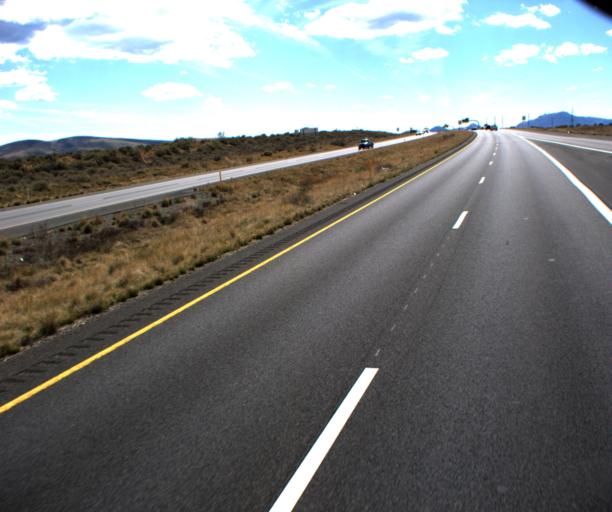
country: US
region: Arizona
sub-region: Yavapai County
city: Prescott Valley
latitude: 34.6400
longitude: -112.3183
